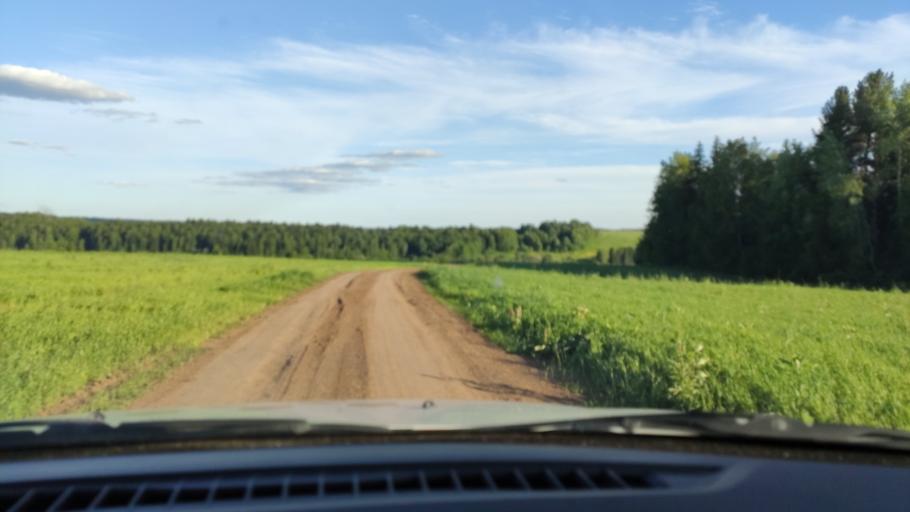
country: RU
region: Perm
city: Orda
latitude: 57.2957
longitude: 56.5946
